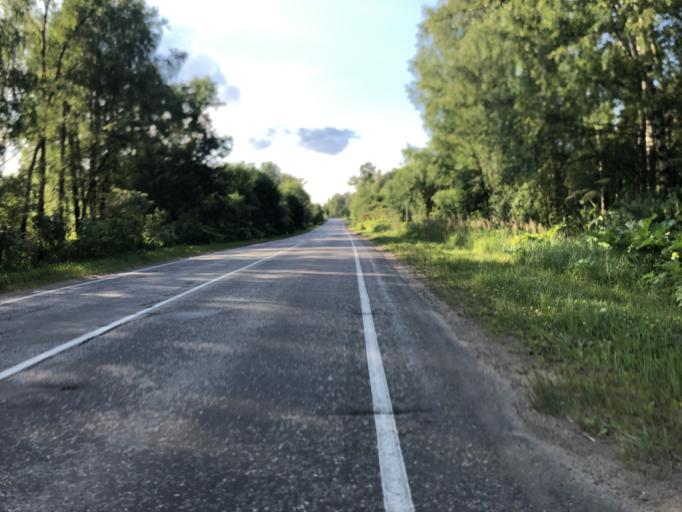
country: RU
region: Tverskaya
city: Rzhev
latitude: 56.2702
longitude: 34.2477
